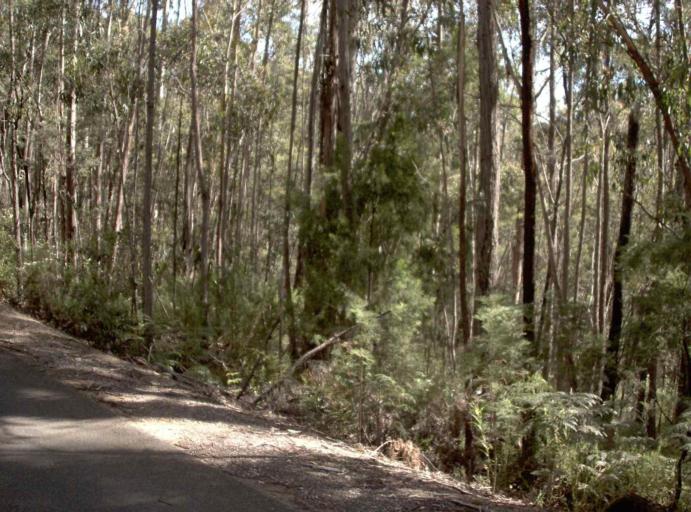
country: AU
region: Victoria
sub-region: East Gippsland
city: Lakes Entrance
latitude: -37.4315
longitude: 148.1282
